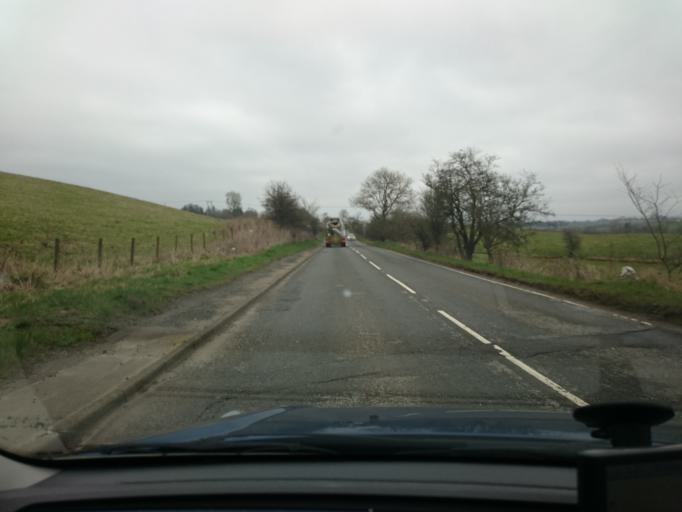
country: GB
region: Scotland
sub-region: North Lanarkshire
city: Cumbernauld
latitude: 55.9850
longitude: -3.9875
